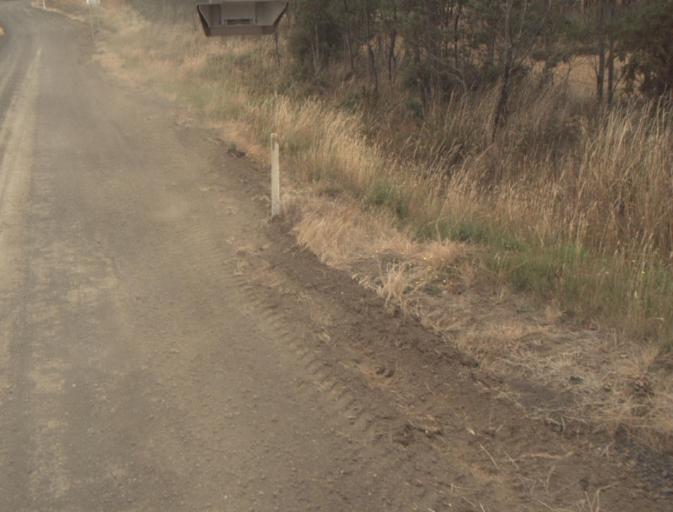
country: AU
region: Tasmania
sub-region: Northern Midlands
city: Evandale
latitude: -41.5232
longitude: 147.3664
